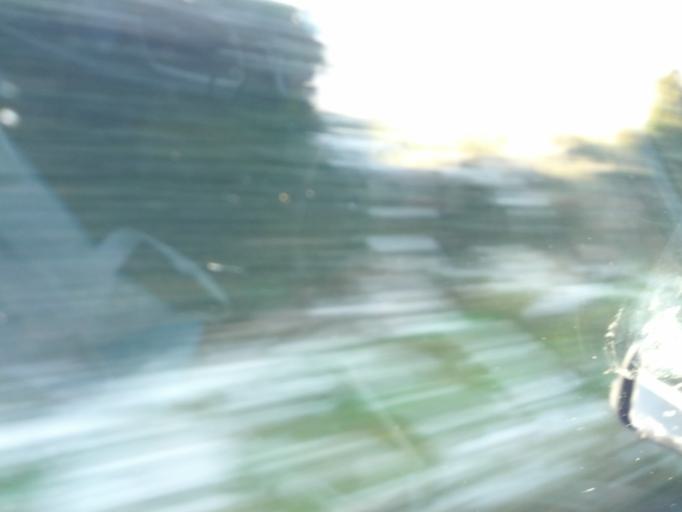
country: IE
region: Connaught
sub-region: County Galway
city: Gort
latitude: 53.1530
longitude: -8.7902
